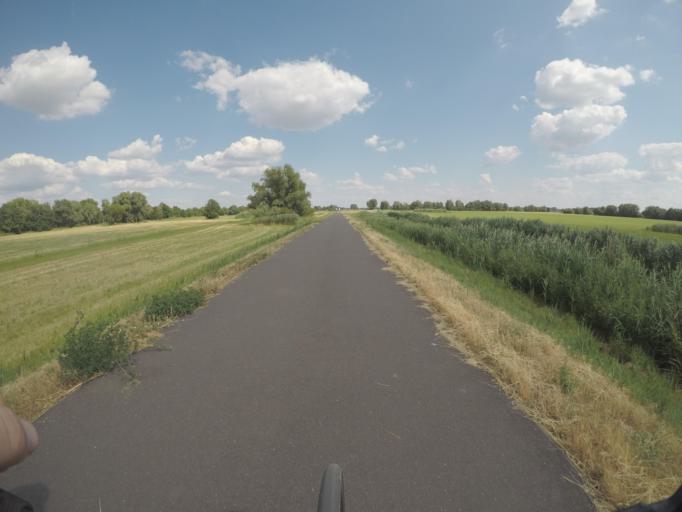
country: DE
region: Brandenburg
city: Ketzin
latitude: 52.4678
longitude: 12.8358
